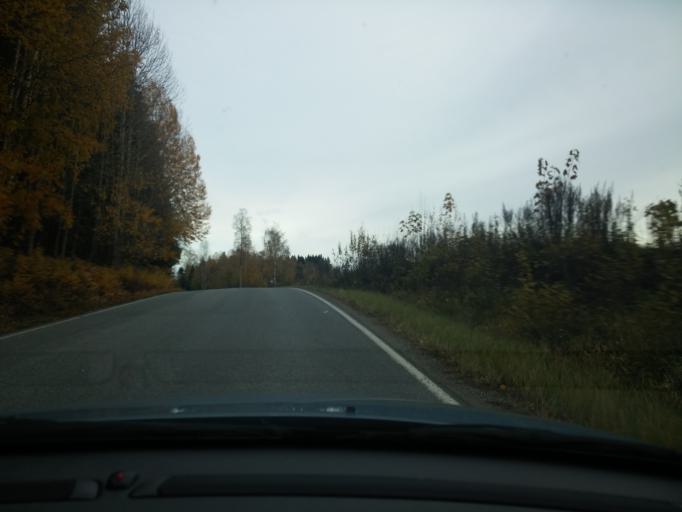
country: FI
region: Haeme
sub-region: Forssa
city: Tammela
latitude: 60.7649
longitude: 23.8636
